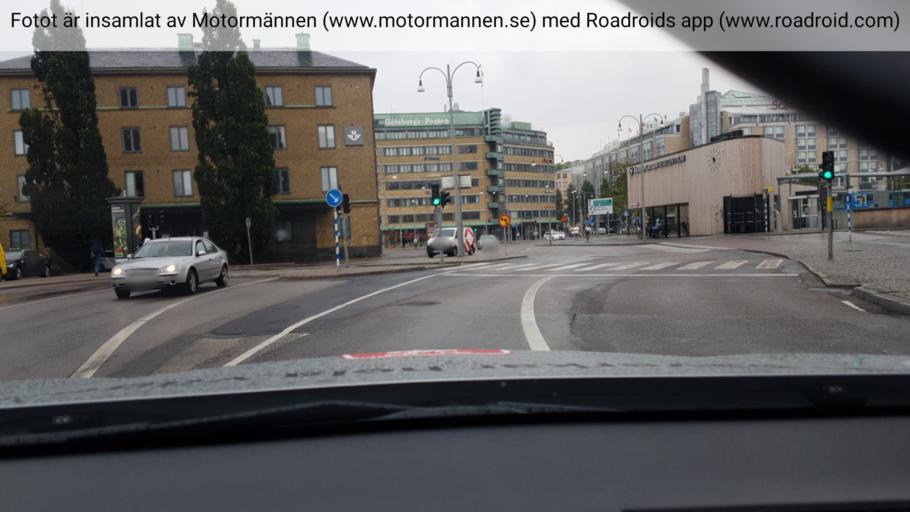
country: SE
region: Vaestra Goetaland
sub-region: Goteborg
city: Goeteborg
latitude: 57.7090
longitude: 11.9758
